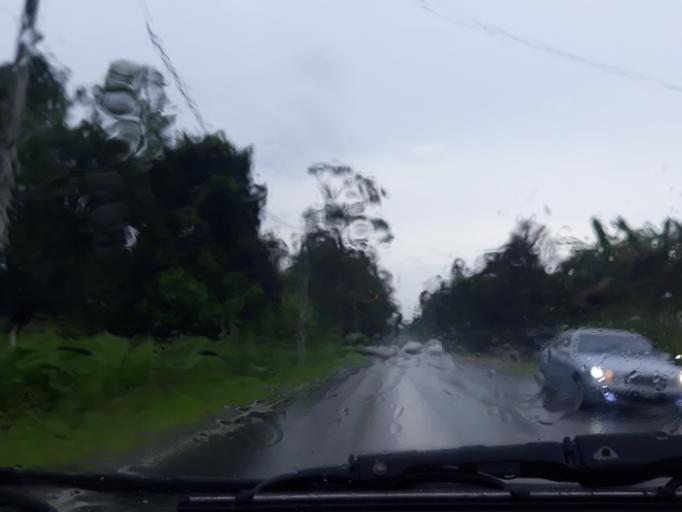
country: MY
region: Kedah
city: Kulim
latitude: 5.3572
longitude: 100.5825
